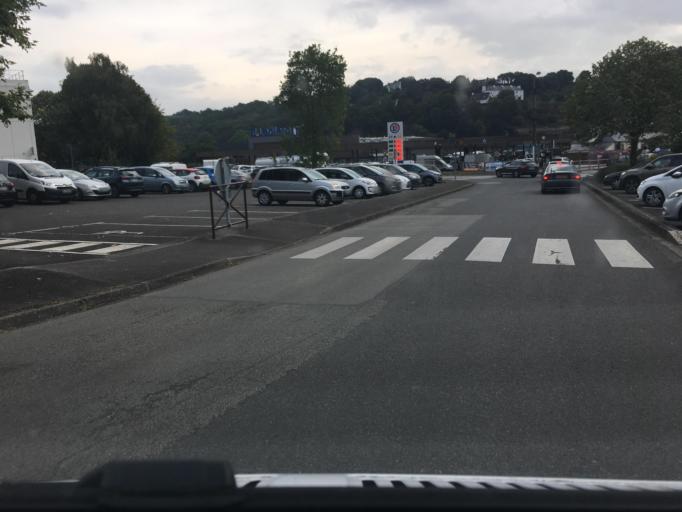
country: FR
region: Brittany
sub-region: Departement du Finistere
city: Chateaulin
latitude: 48.2001
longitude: -4.0893
